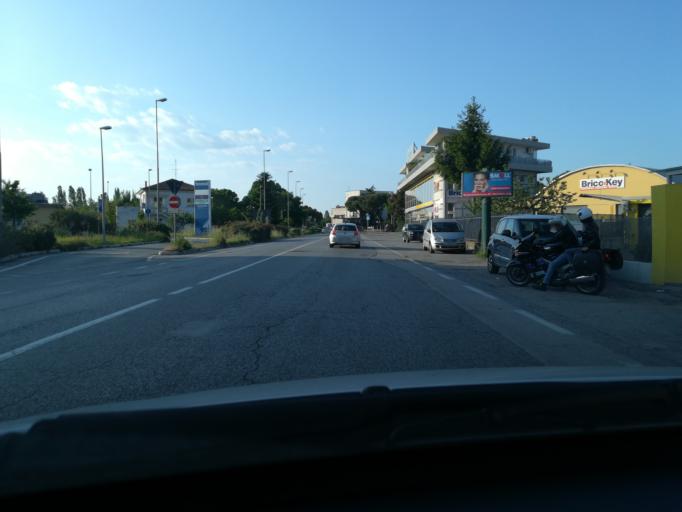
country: IT
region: Emilia-Romagna
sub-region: Provincia di Rimini
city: Riccione
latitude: 43.9962
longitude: 12.6484
